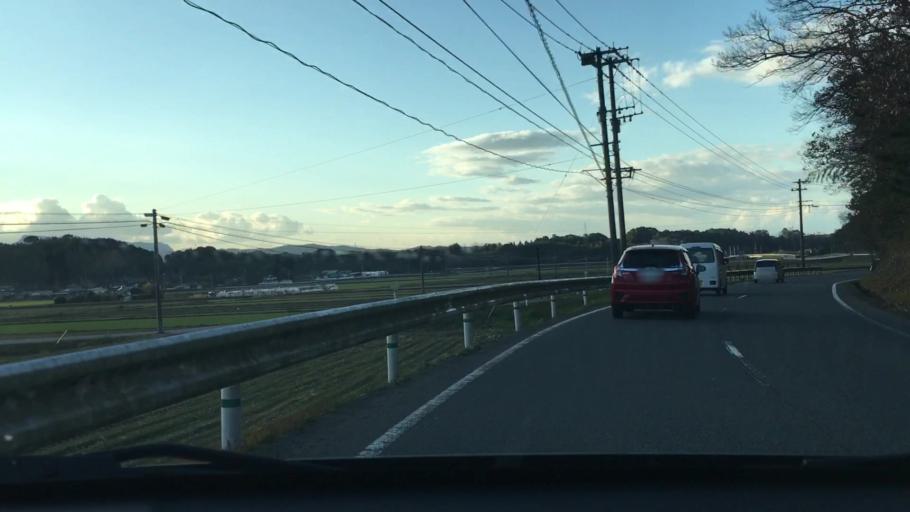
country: JP
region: Oita
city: Bungo-Takada-shi
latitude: 33.5081
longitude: 131.3599
